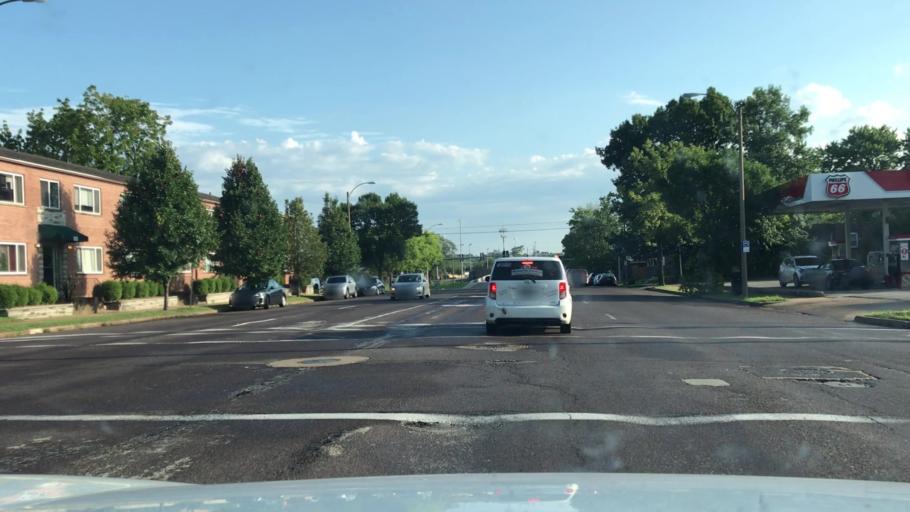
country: US
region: Missouri
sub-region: Saint Louis County
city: Maplewood
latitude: 38.6035
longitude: -90.3077
